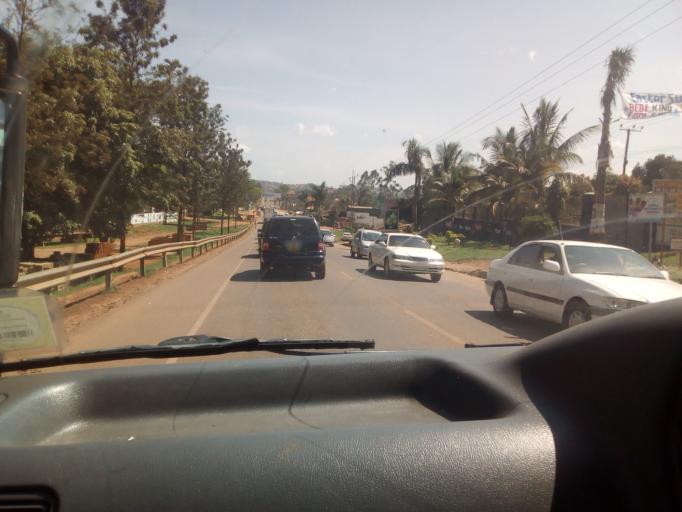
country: UG
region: Central Region
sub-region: Wakiso District
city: Kajansi
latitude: 0.2290
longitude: 32.5503
